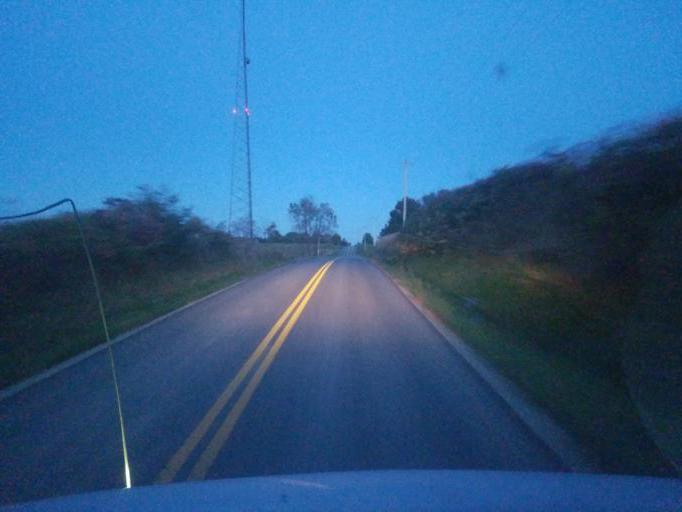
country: US
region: Ohio
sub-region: Perry County
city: Somerset
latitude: 39.8605
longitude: -82.2338
